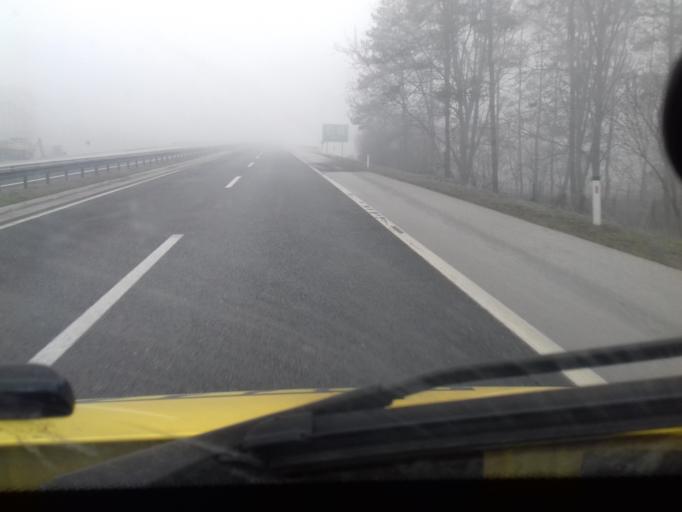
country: BA
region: Federation of Bosnia and Herzegovina
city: Visoko
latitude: 43.9964
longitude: 18.1869
